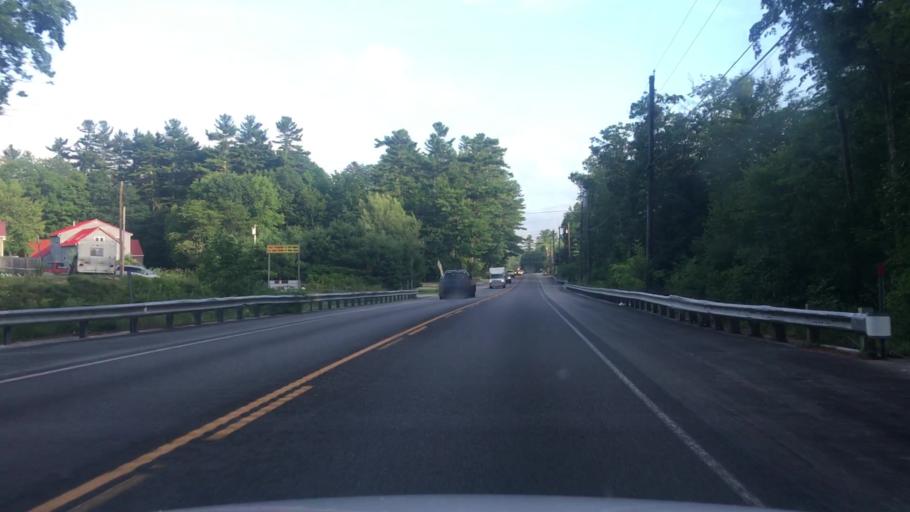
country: US
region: Maine
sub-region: Cumberland County
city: North Windham
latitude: 43.7933
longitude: -70.3985
